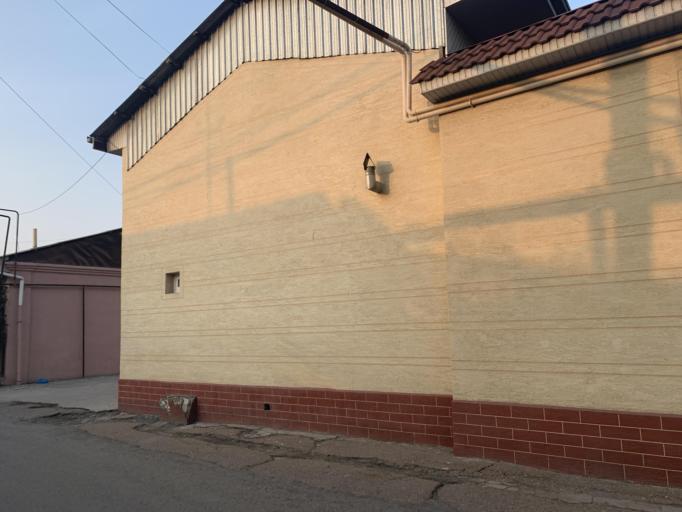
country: UZ
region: Fergana
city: Qo`qon
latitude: 40.5318
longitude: 70.9311
